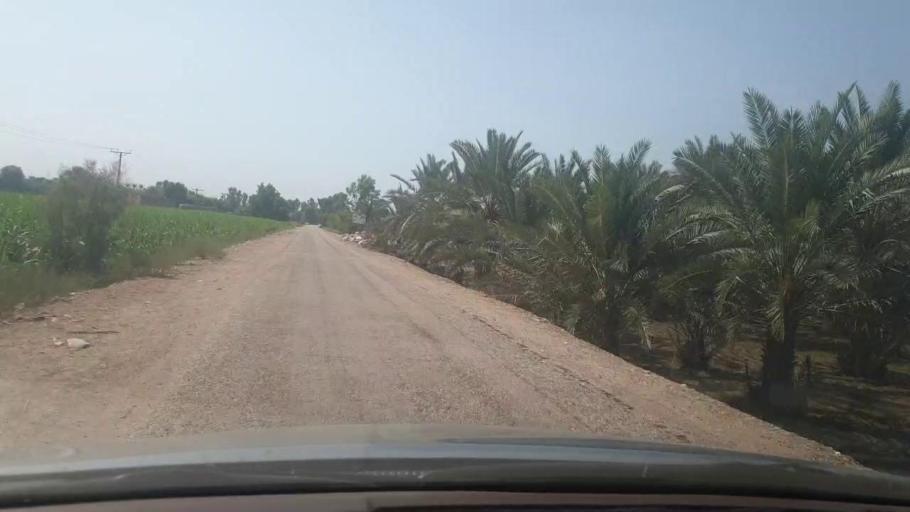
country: PK
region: Sindh
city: Ranipur
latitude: 27.2850
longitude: 68.5795
